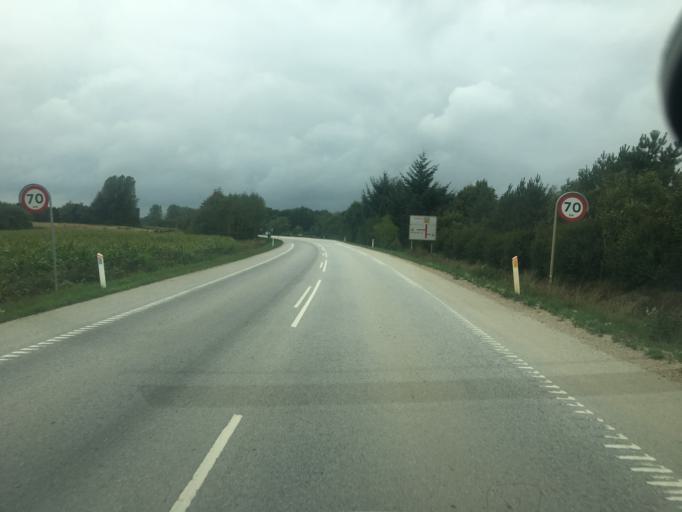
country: DK
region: South Denmark
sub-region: Haderslev Kommune
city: Vojens
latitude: 55.2347
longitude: 9.2973
